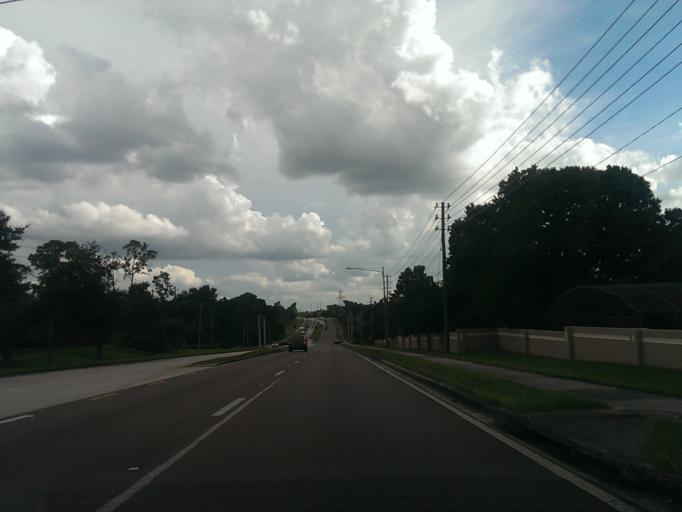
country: US
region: Florida
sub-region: Orange County
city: Bay Hill
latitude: 28.4859
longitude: -81.5087
